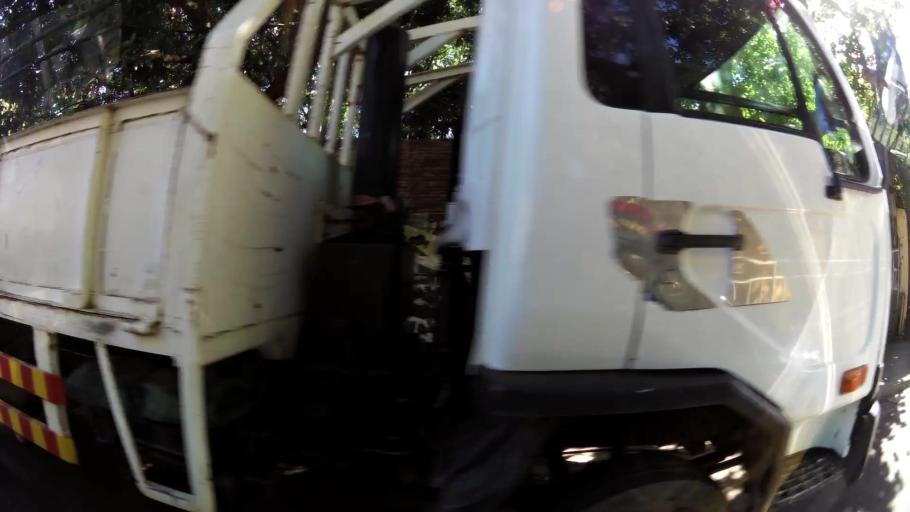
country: MU
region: Grand Port
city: Mahebourg
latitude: -20.4085
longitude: 57.7083
